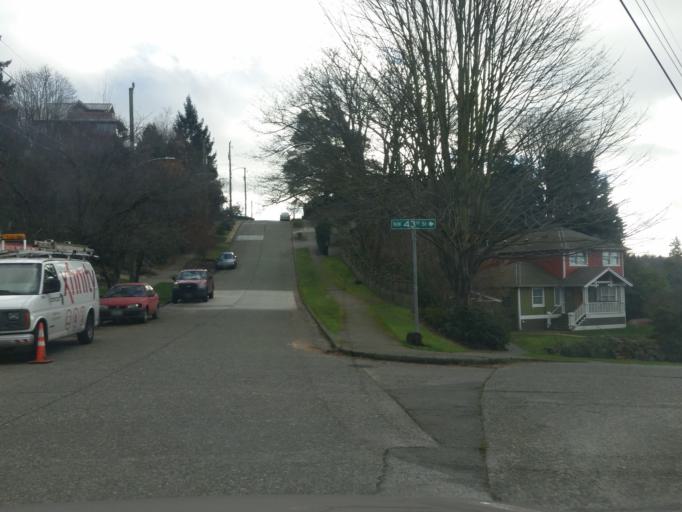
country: US
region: Washington
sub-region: King County
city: Seattle
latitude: 47.6595
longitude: -122.3573
